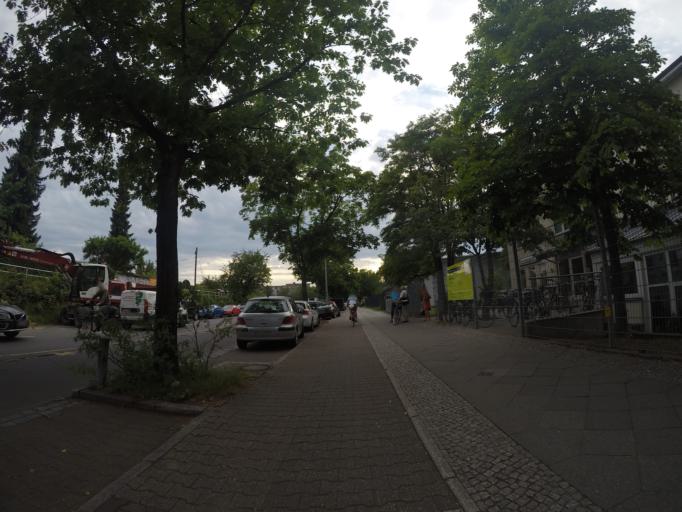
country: DE
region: Berlin
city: Halensee
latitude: 52.4805
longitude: 13.3013
